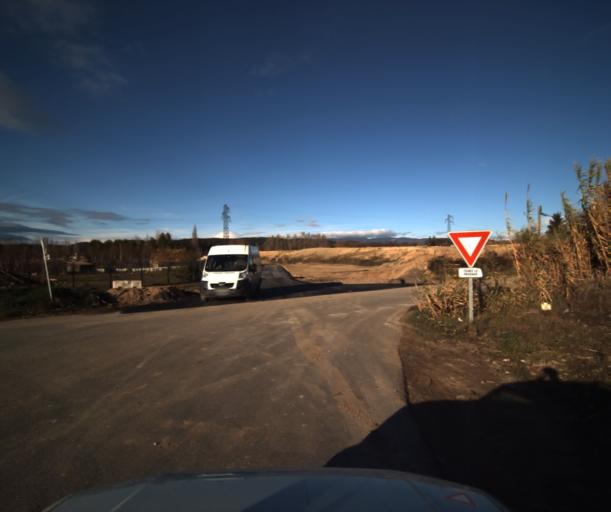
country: FR
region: Provence-Alpes-Cote d'Azur
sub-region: Departement du Vaucluse
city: Pertuis
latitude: 43.6896
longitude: 5.4825
